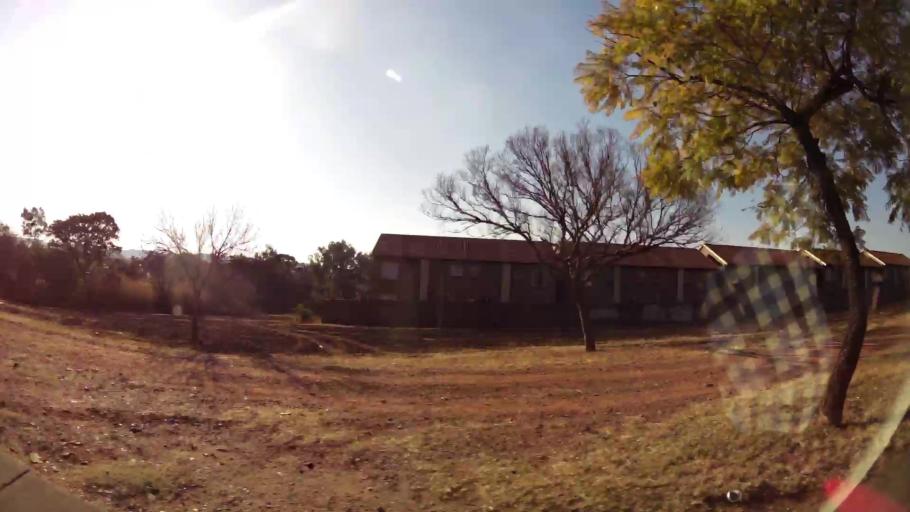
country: ZA
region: Gauteng
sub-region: City of Tshwane Metropolitan Municipality
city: Pretoria
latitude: -25.7499
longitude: 28.1362
